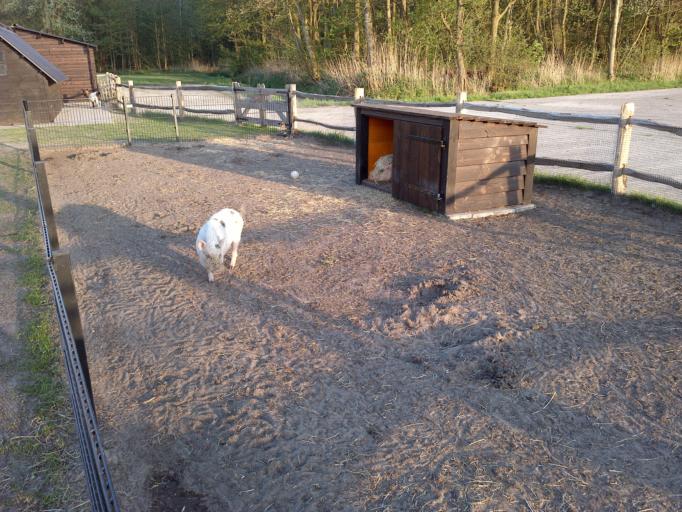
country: NL
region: South Holland
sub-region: Gemeente Lisse
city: Lisse
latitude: 52.2664
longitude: 4.5383
